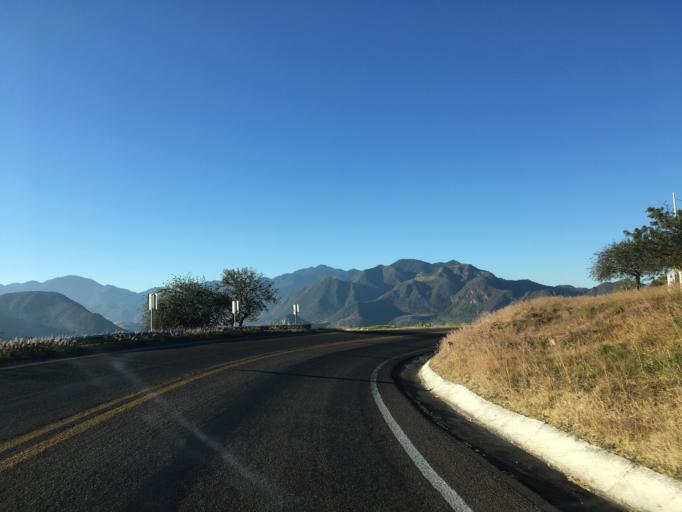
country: MX
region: Michoacan
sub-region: Tuxpan
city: La Soledad
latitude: 19.5209
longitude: -100.4723
